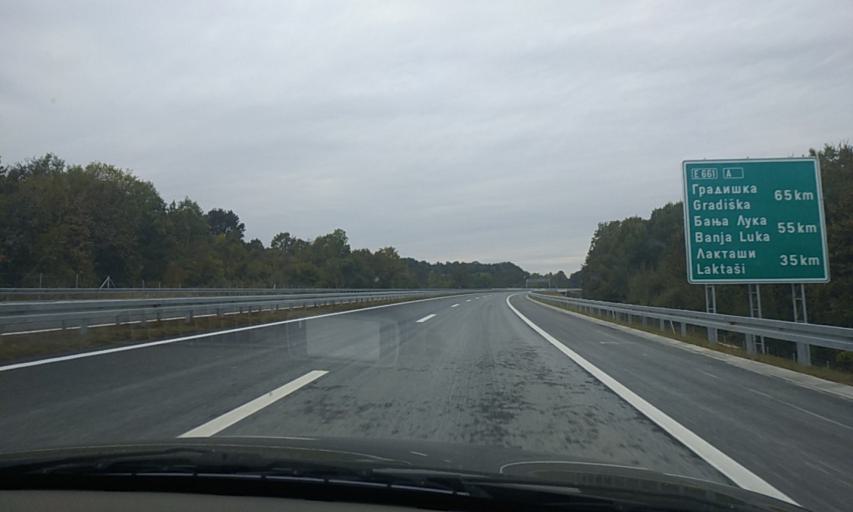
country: BA
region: Republika Srpska
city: Prnjavor
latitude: 44.8505
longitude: 17.6681
